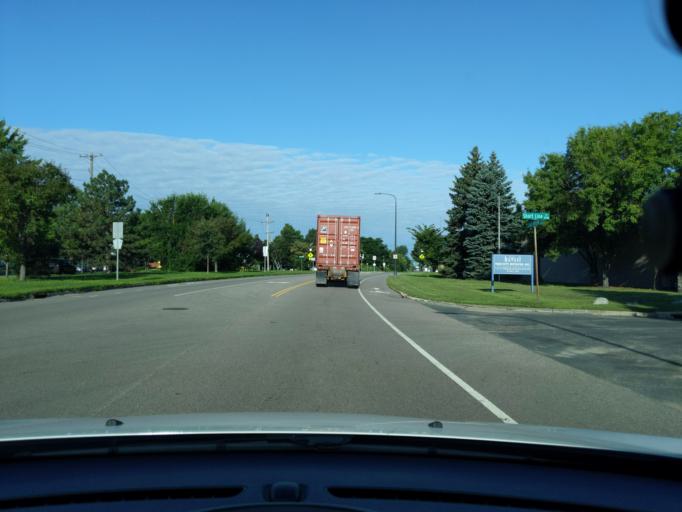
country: US
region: Minnesota
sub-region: Ramsey County
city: Falcon Heights
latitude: 44.9677
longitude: -93.1554
